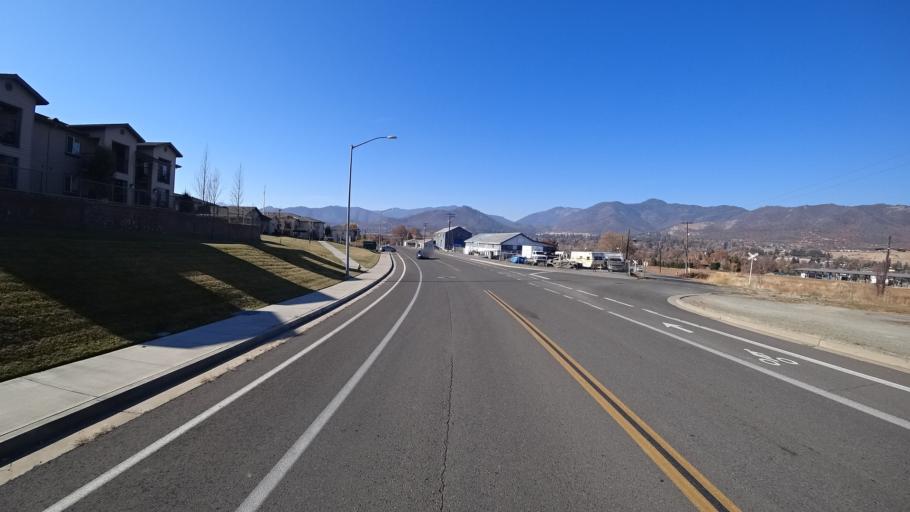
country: US
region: California
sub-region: Siskiyou County
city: Yreka
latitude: 41.7347
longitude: -122.6252
